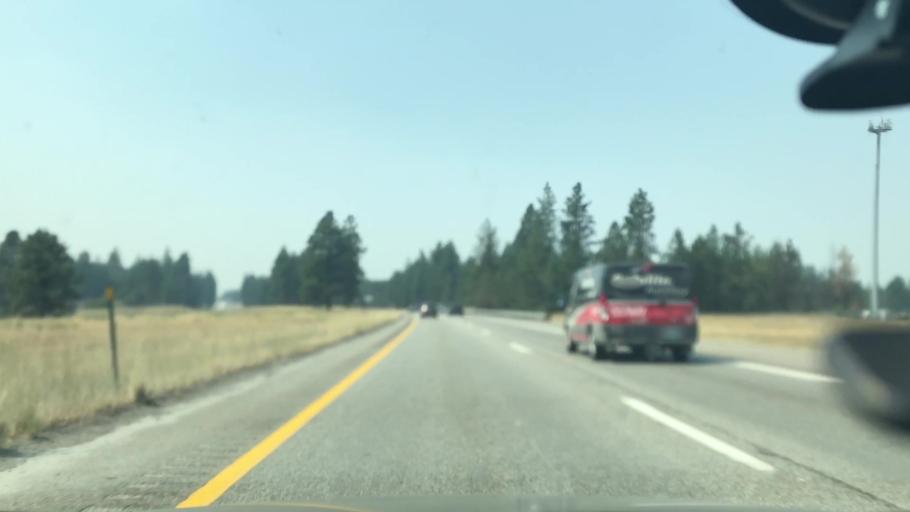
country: US
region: Idaho
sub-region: Kootenai County
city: Coeur d'Alene
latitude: 47.7081
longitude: -116.8521
